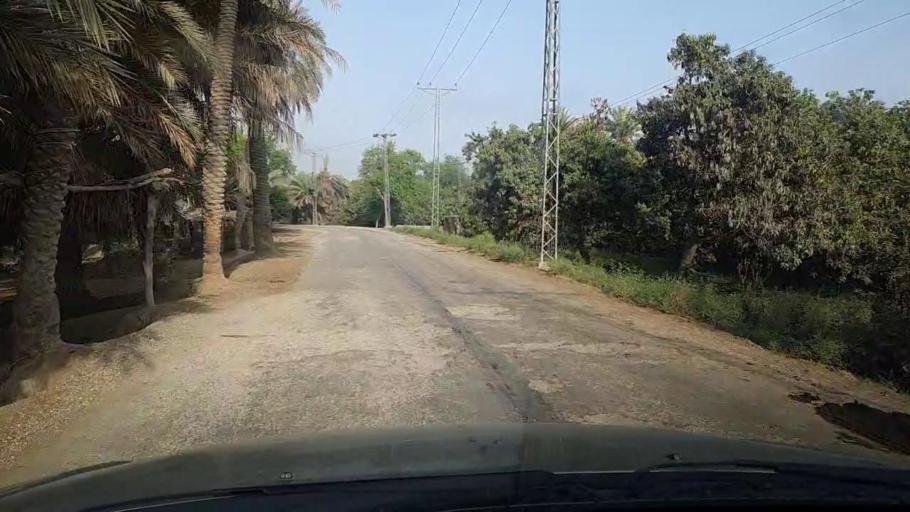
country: PK
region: Sindh
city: Pir jo Goth
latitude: 27.5719
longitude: 68.6209
